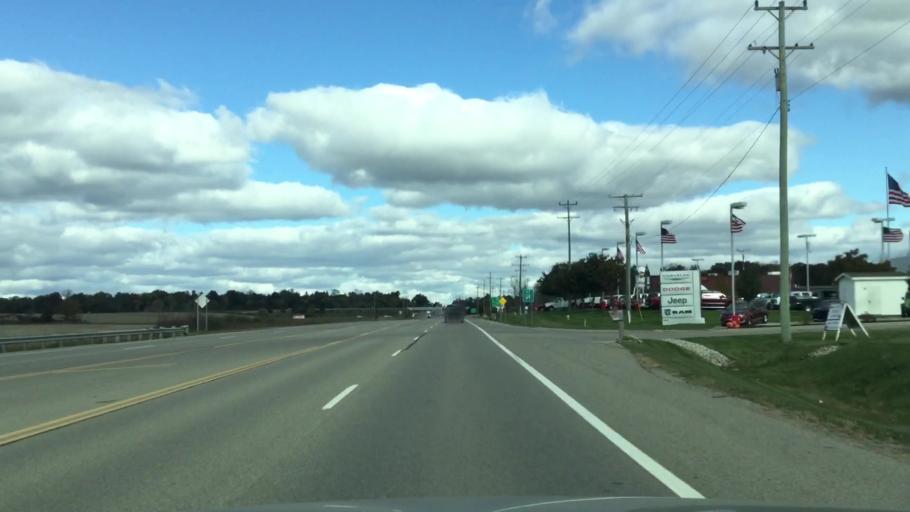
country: US
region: Michigan
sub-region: Lapeer County
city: Lapeer
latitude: 43.0165
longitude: -83.3220
